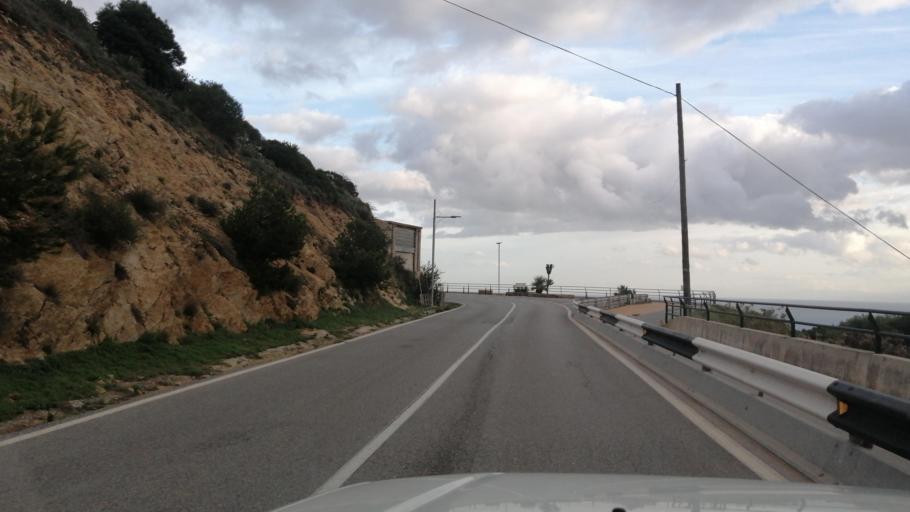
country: ES
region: Ceuta
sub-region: Ceuta
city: Ceuta
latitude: 35.8980
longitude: -5.2814
